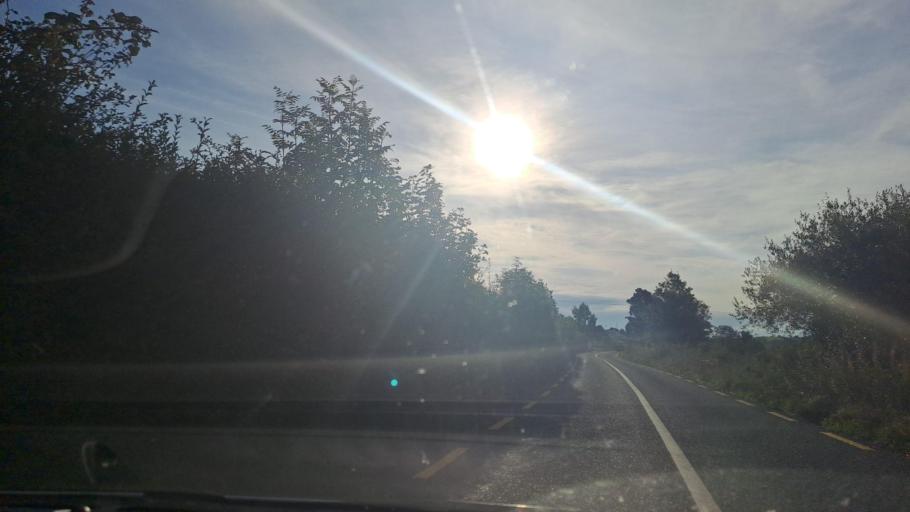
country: IE
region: Ulster
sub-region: An Cabhan
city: Kingscourt
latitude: 53.9757
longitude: -6.8750
